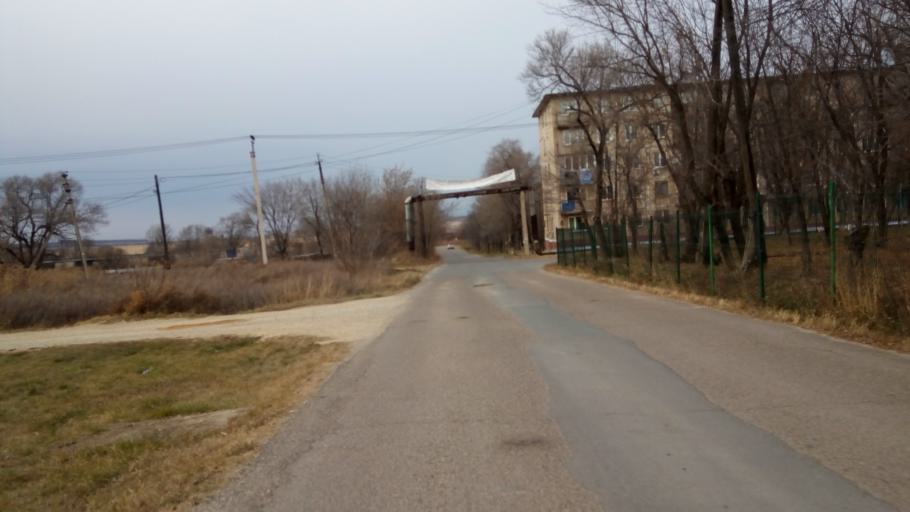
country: RU
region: Primorskiy
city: Novoshakhtinskiy
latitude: 44.0247
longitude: 132.1614
